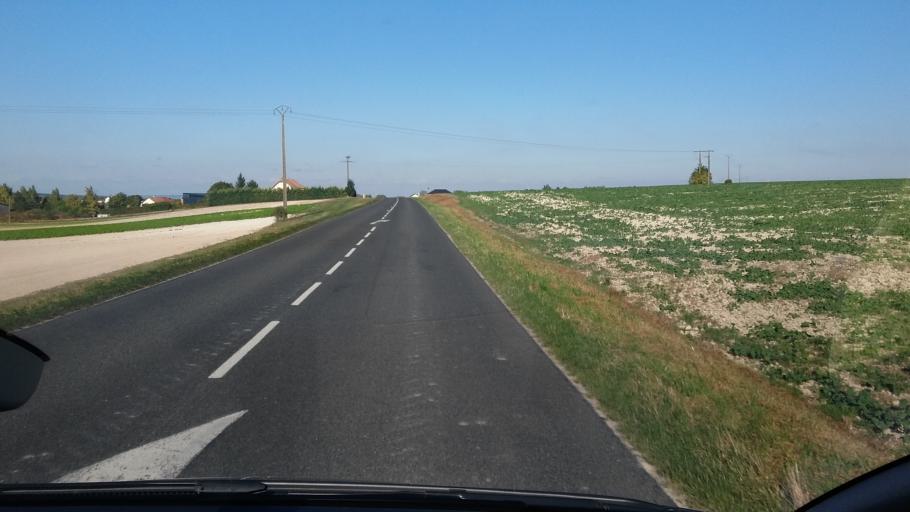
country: FR
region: Champagne-Ardenne
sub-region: Departement de la Marne
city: Vertus
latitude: 48.8707
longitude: 3.9934
